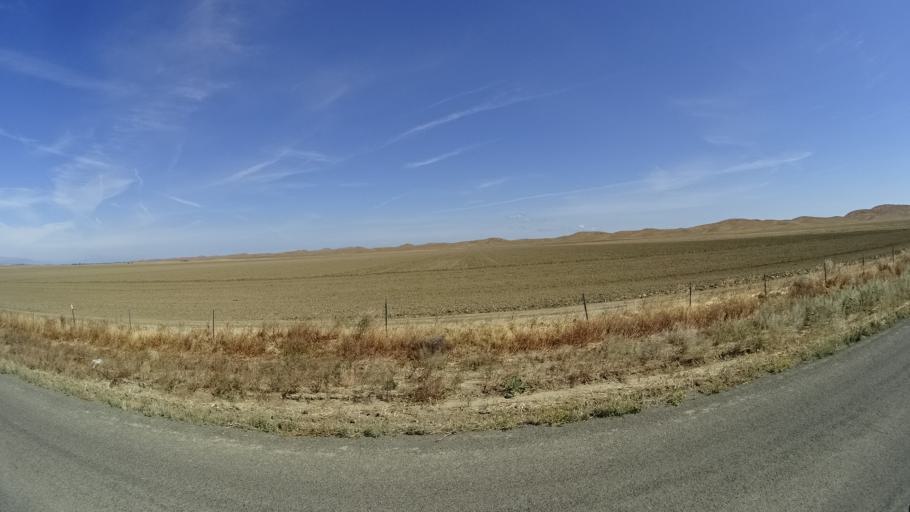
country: US
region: California
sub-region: Kings County
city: Kettleman City
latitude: 35.9353
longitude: -120.0315
